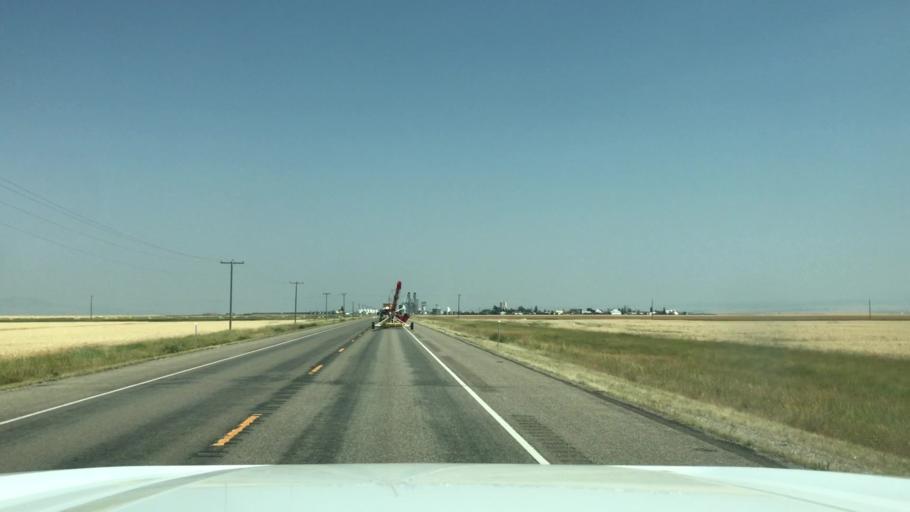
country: US
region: Montana
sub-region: Judith Basin County
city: Stanford
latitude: 47.0552
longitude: -109.9299
